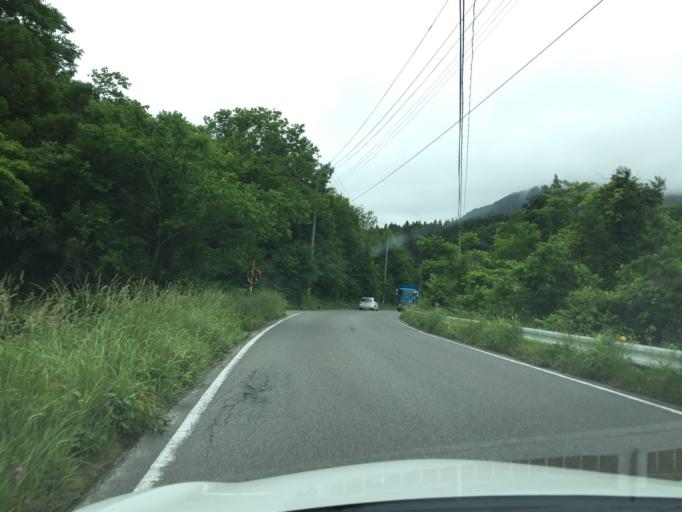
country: JP
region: Fukushima
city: Funehikimachi-funehiki
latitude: 37.3276
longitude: 140.6976
